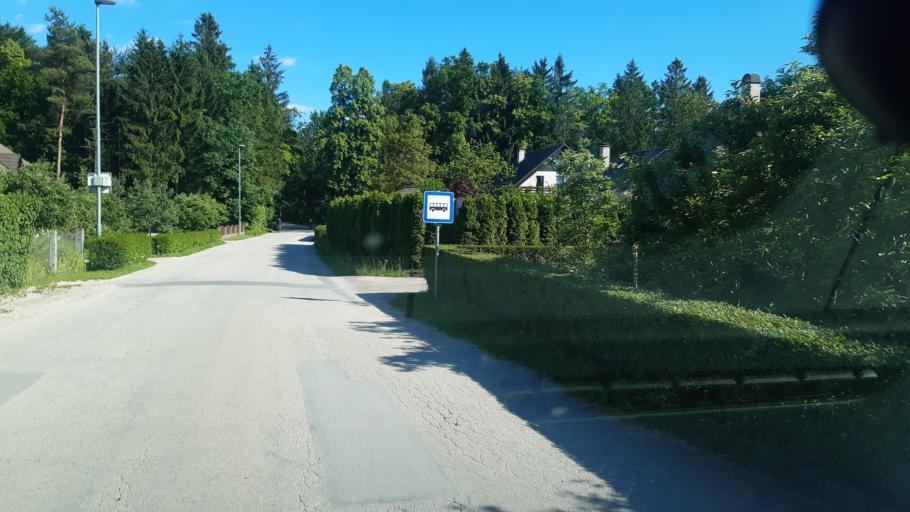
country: SI
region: Sencur
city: Hrastje
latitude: 46.2085
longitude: 14.3910
